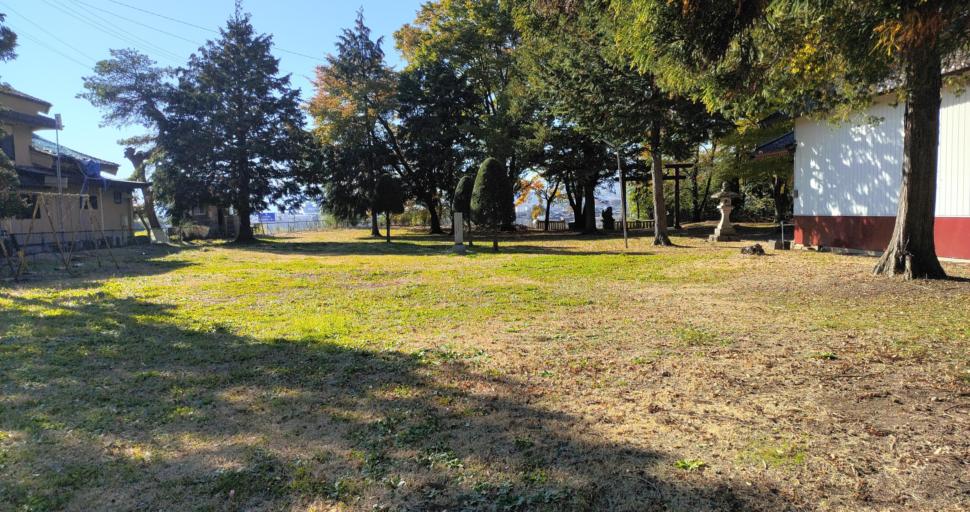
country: JP
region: Nagano
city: Saku
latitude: 36.2444
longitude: 138.4759
